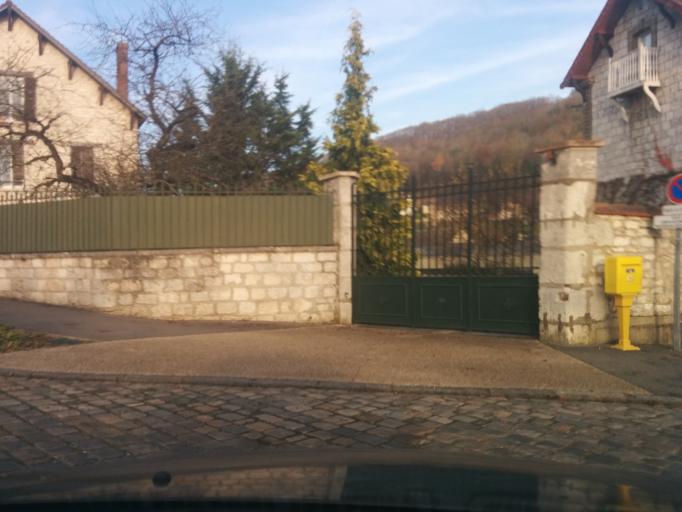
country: FR
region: Haute-Normandie
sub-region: Departement de l'Eure
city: Vernon
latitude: 49.1025
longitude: 1.4858
